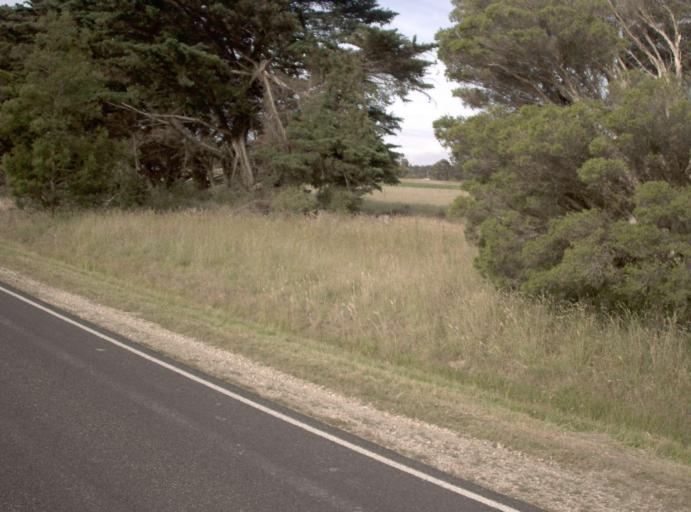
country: AU
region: Victoria
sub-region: Wellington
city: Heyfield
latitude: -38.0151
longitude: 146.6711
